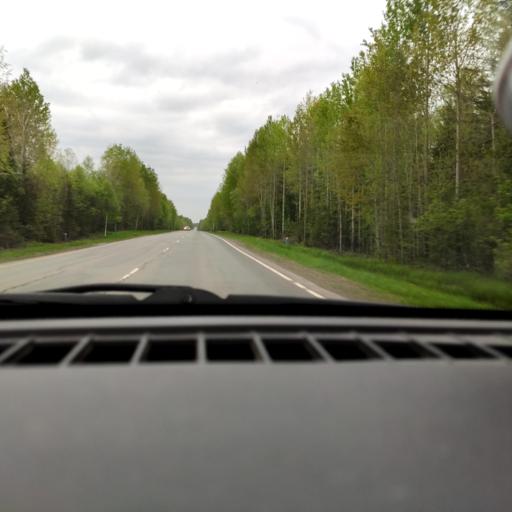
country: RU
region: Perm
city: Polazna
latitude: 58.2699
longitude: 56.1672
